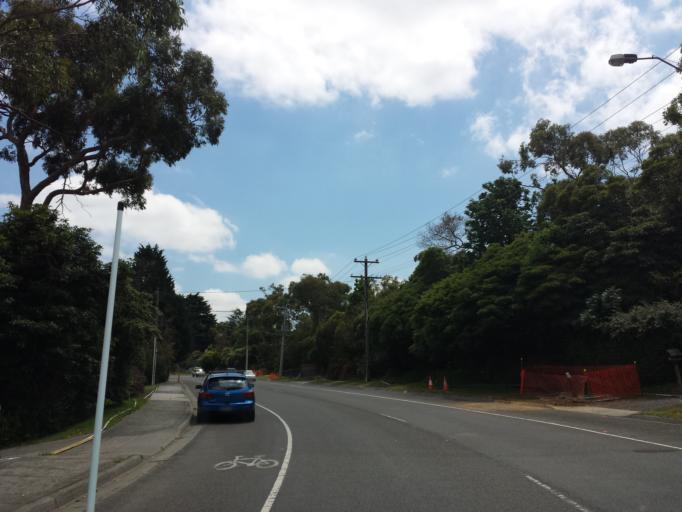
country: AU
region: Victoria
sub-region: Knox
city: Boronia
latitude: -37.8692
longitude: 145.2974
